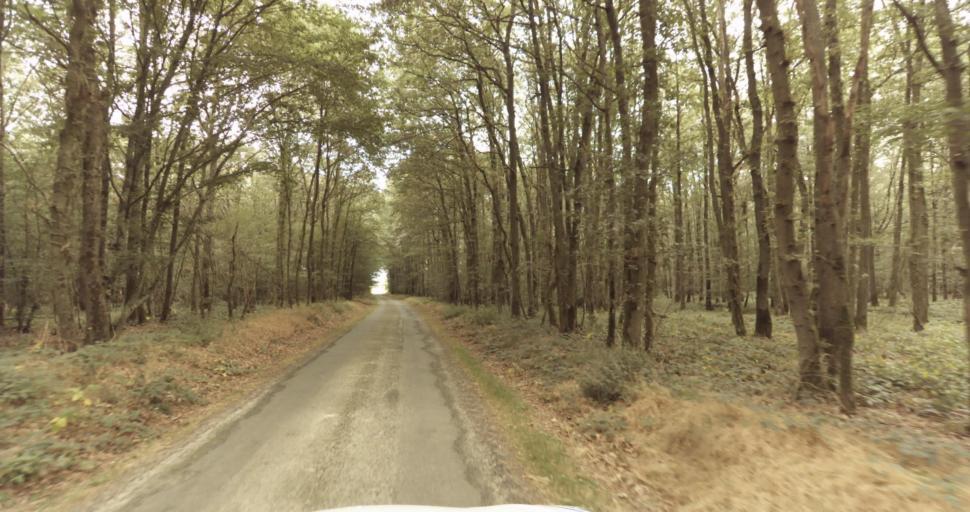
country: FR
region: Haute-Normandie
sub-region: Departement de l'Eure
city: Tillieres-sur-Avre
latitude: 48.7869
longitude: 1.1193
